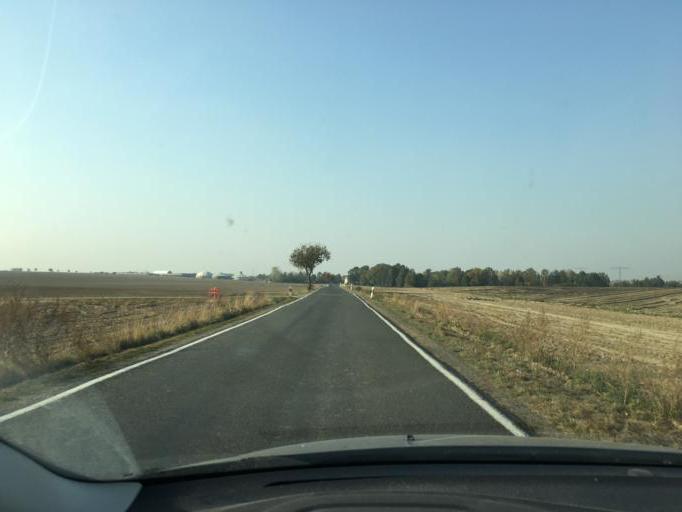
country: DE
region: Saxony
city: Wurzen
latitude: 51.3359
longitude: 12.7753
